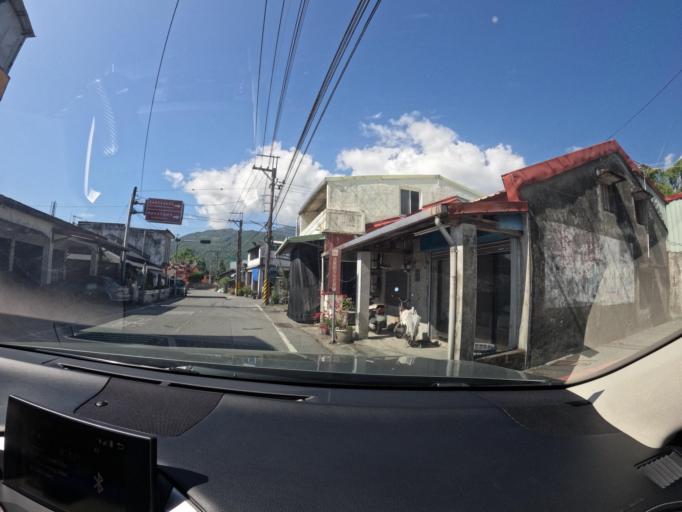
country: TW
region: Taiwan
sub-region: Hualien
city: Hualian
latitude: 23.5773
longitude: 121.3763
